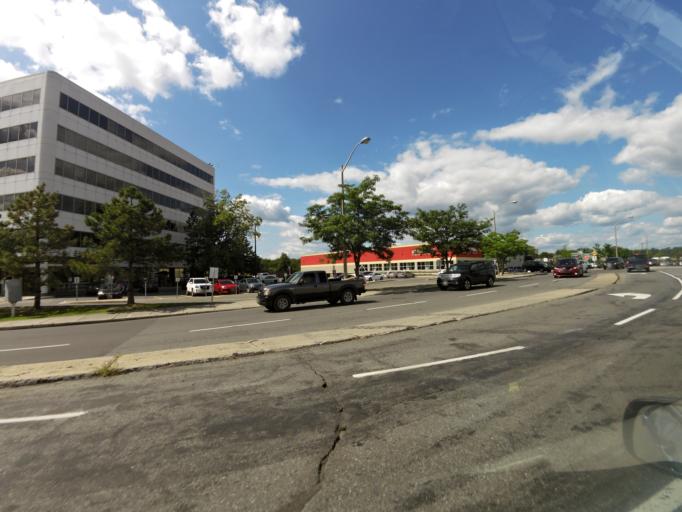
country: CA
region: Ontario
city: Bells Corners
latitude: 45.3483
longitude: -75.7872
